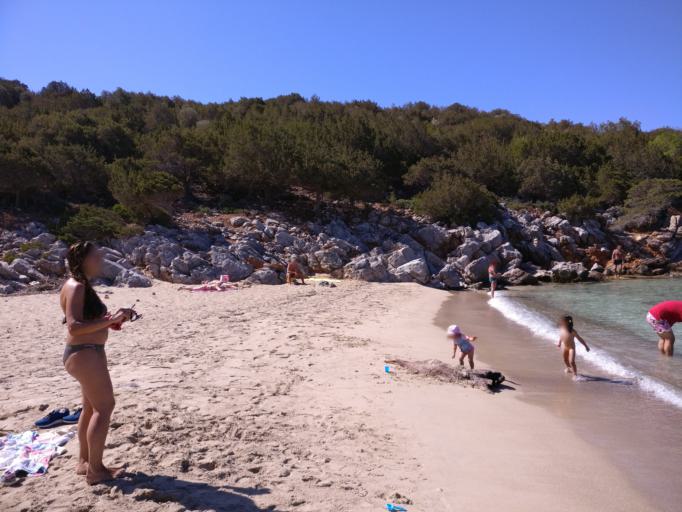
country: GR
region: North Aegean
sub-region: Nomos Samou
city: Chora
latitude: 37.6306
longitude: 26.7892
